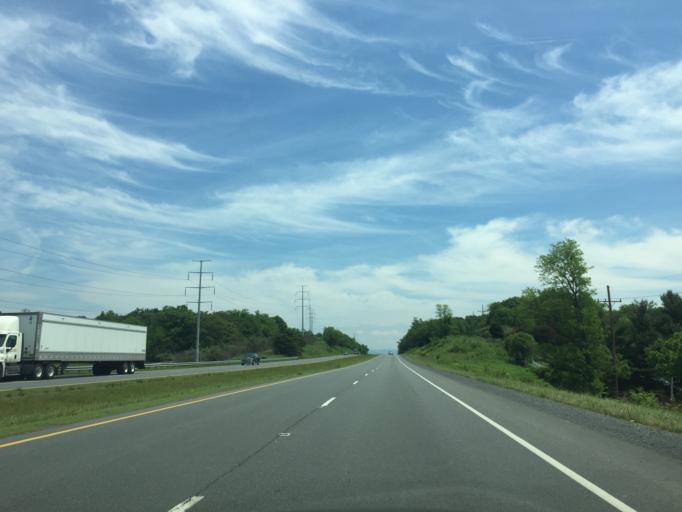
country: US
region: Virginia
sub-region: City of Winchester
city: Winchester
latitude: 39.2129
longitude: -78.1703
